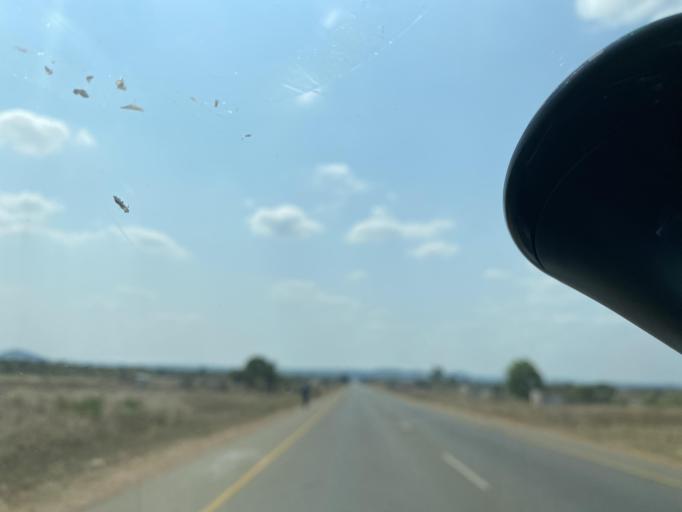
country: ZM
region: Lusaka
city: Chongwe
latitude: -15.5692
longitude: 28.6939
